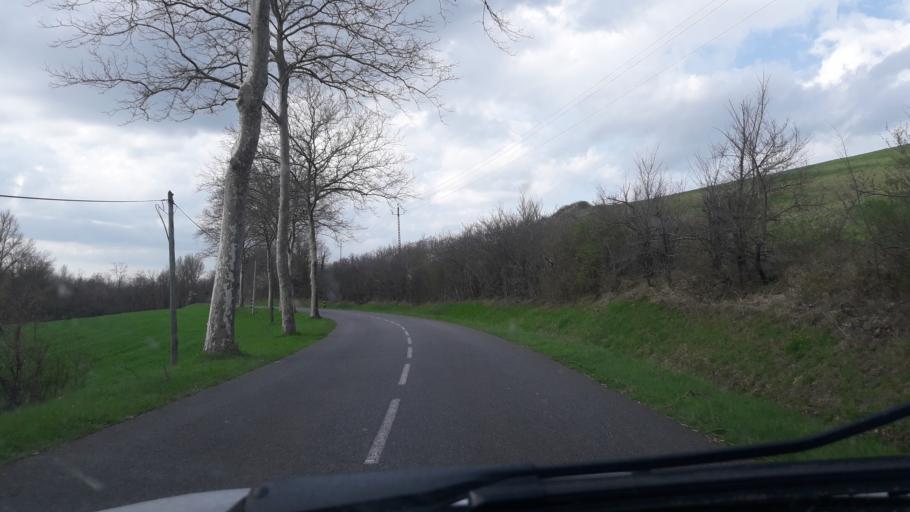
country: FR
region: Midi-Pyrenees
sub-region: Departement de la Haute-Garonne
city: Rieux-Volvestre
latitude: 43.2531
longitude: 1.2492
